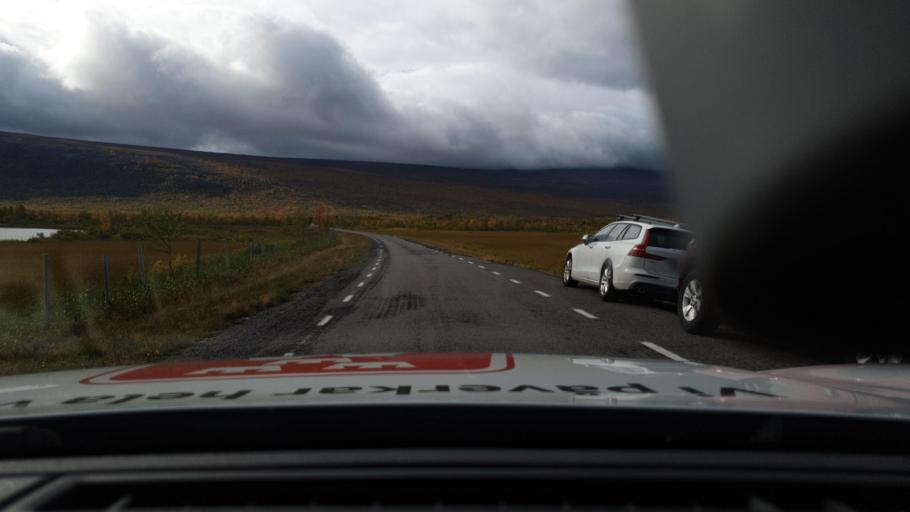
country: SE
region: Norrbotten
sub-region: Kiruna Kommun
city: Kiruna
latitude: 67.8602
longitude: 19.0277
